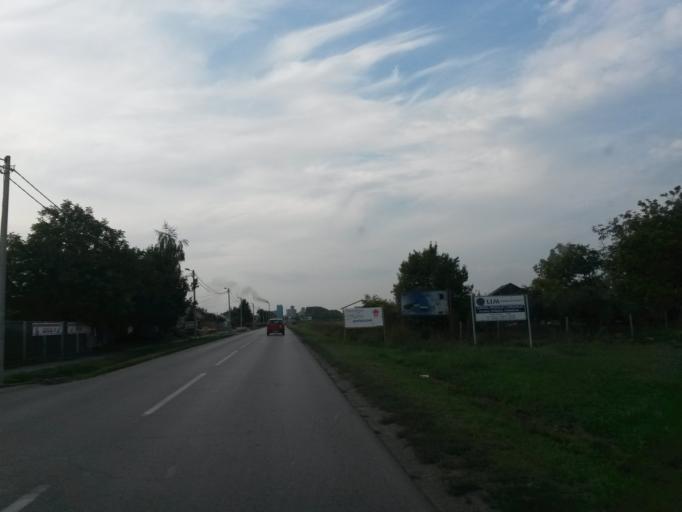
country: HR
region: Osjecko-Baranjska
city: Tenja
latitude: 45.5420
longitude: 18.7568
